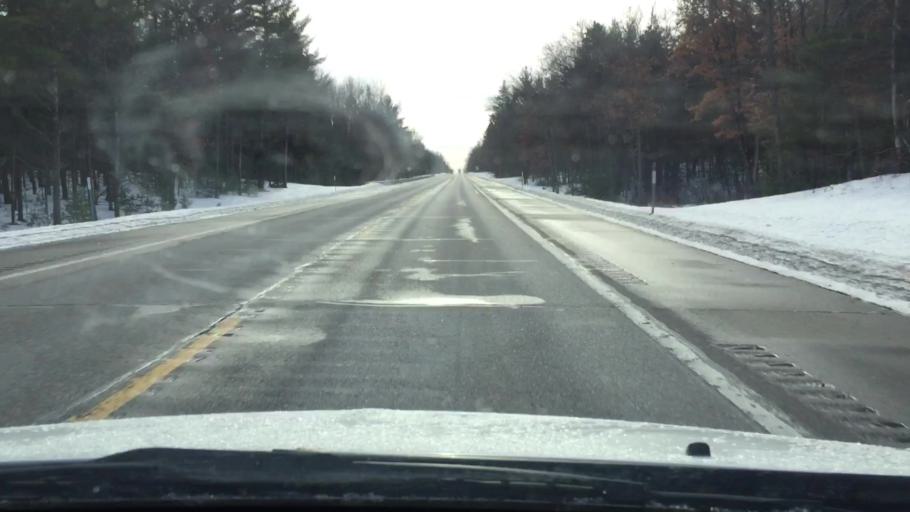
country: US
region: Michigan
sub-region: Wexford County
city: Manton
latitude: 44.5438
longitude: -85.3724
